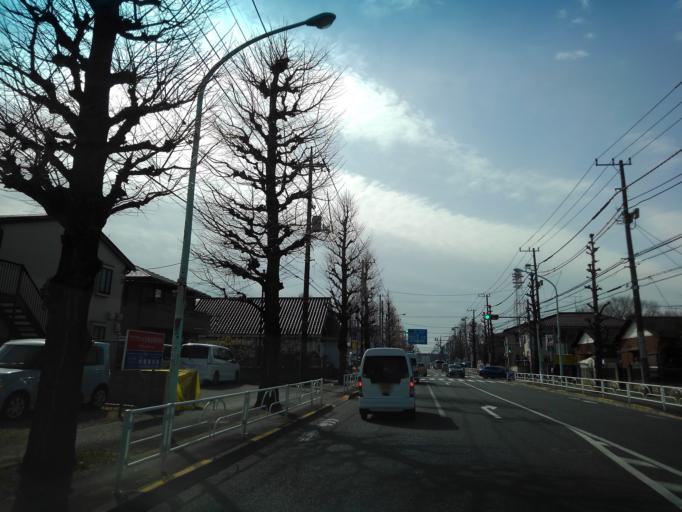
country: JP
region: Tokyo
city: Tanashicho
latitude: 35.7427
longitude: 139.5023
